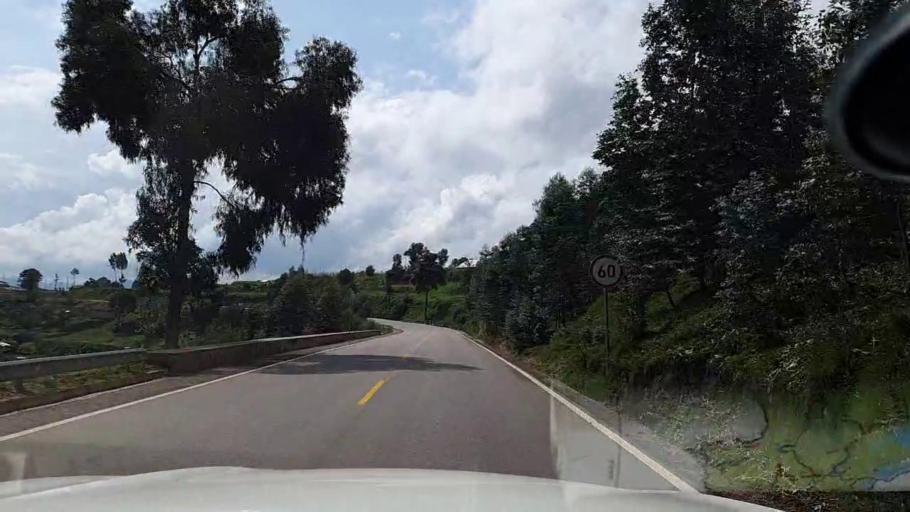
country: RW
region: Southern Province
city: Nzega
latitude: -2.4999
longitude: 29.5079
